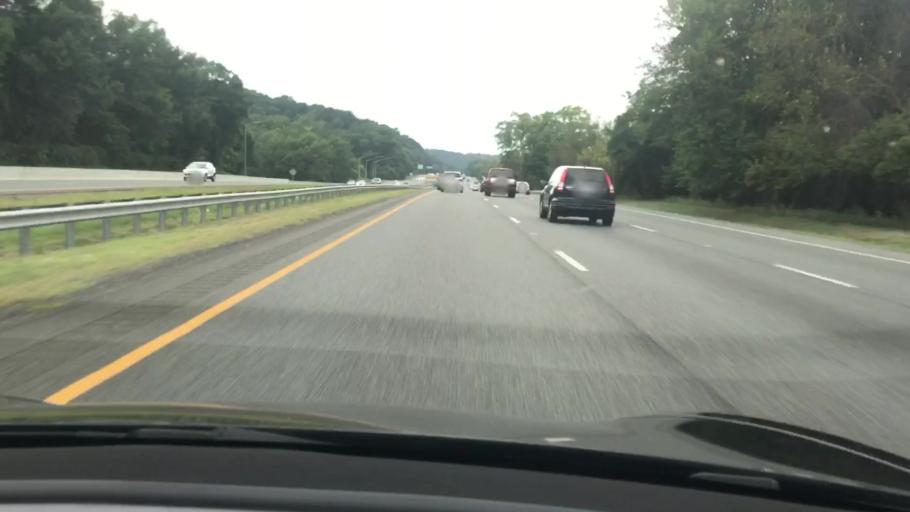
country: US
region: Maryland
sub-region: Baltimore County
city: Mays Chapel
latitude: 39.4533
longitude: -76.6437
